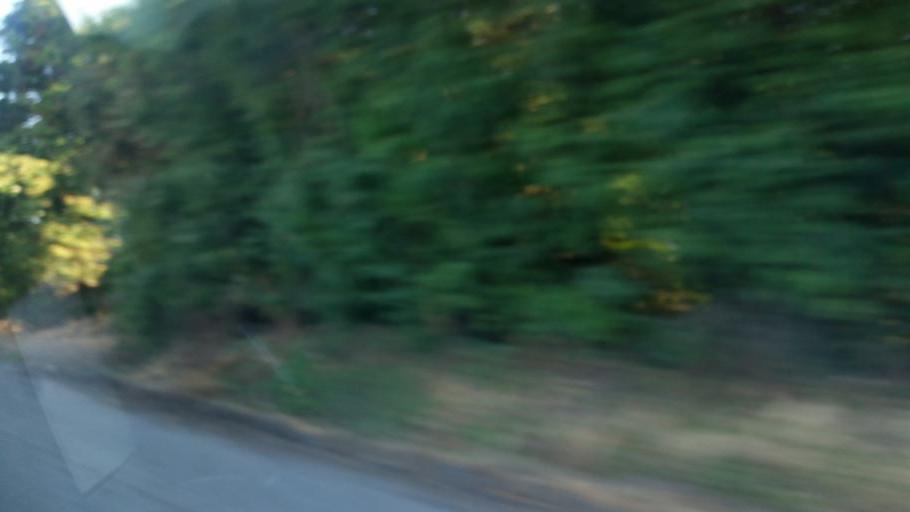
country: IE
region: Leinster
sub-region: Fingal County
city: Blanchardstown
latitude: 53.4529
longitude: -6.3465
